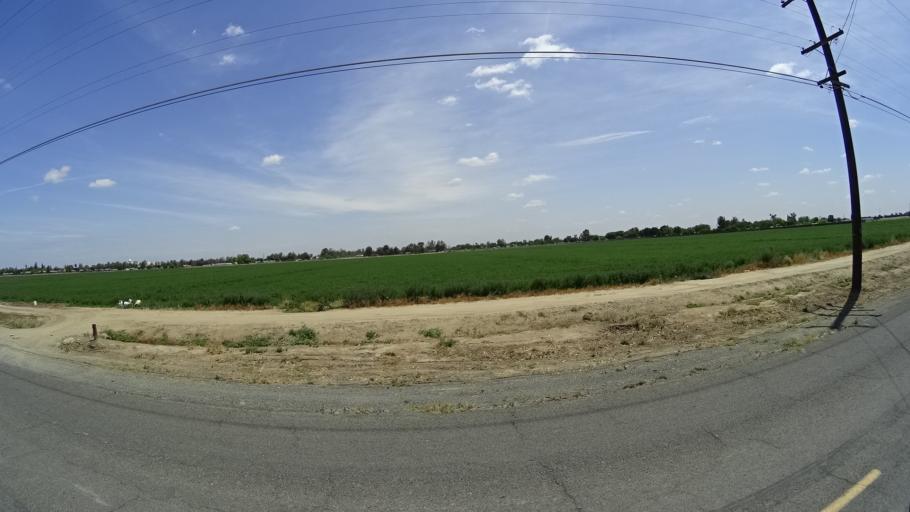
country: US
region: California
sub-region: Kings County
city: Home Garden
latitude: 36.3043
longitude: -119.6460
